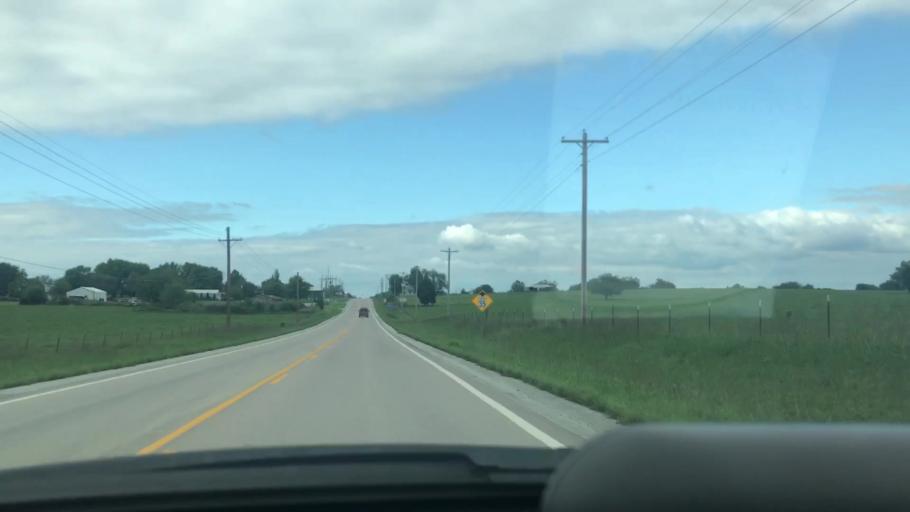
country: US
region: Missouri
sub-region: Hickory County
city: Hermitage
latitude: 37.9346
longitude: -93.2084
